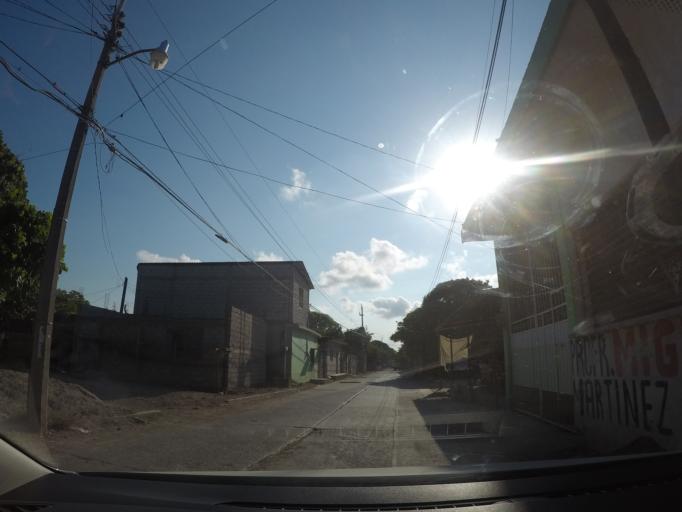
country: MX
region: Oaxaca
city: Juchitan de Zaragoza
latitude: 16.4217
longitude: -95.0258
